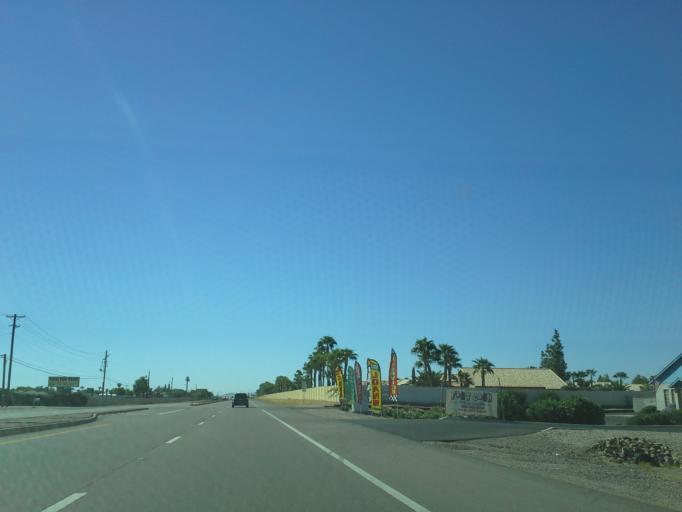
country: US
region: Arizona
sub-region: Maricopa County
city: Sun Lakes
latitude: 33.2122
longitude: -111.8413
